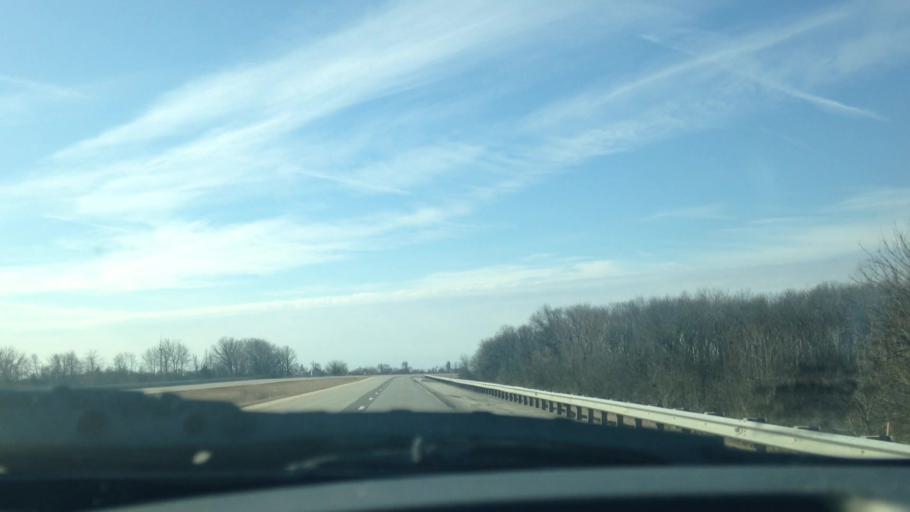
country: US
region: Illinois
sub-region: Ford County
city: Paxton
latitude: 40.5129
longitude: -88.0843
